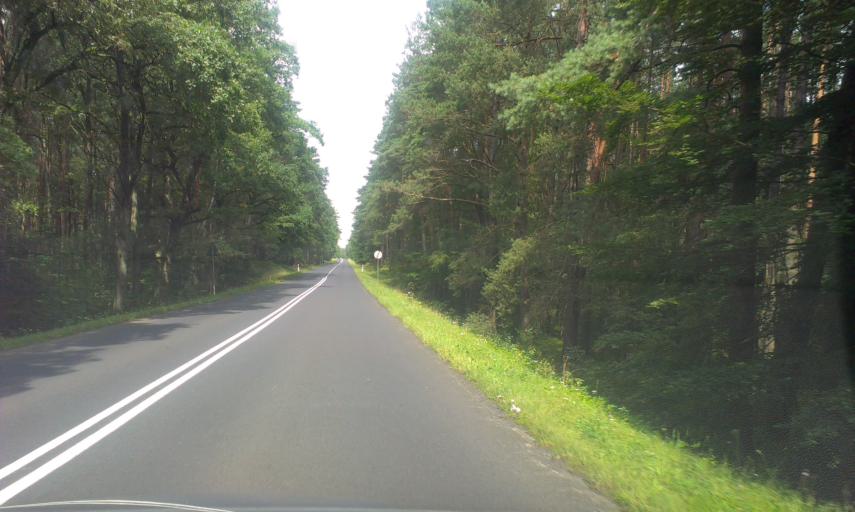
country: PL
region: West Pomeranian Voivodeship
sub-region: Powiat bialogardzki
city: Bialogard
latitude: 53.9360
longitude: 16.0614
